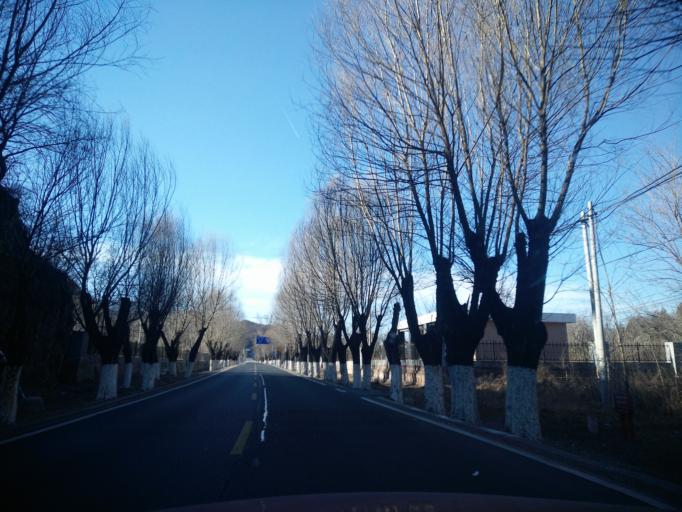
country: CN
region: Beijing
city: Yanchi
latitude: 40.0003
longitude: 115.7753
